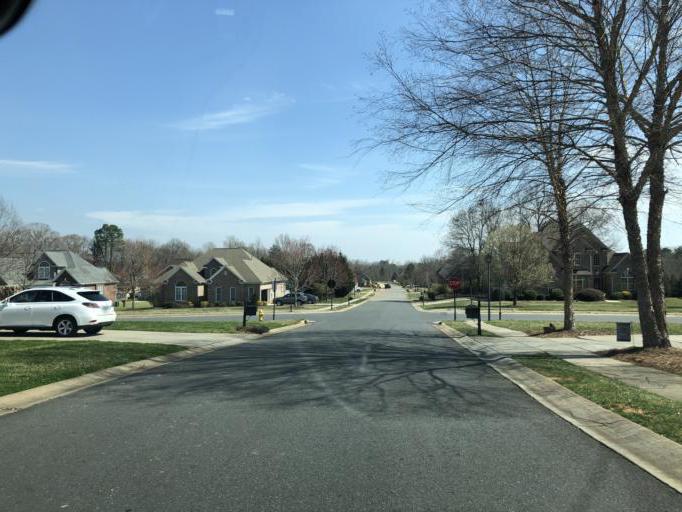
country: US
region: North Carolina
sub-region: Gaston County
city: Stanley
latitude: 35.3428
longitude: -81.0910
